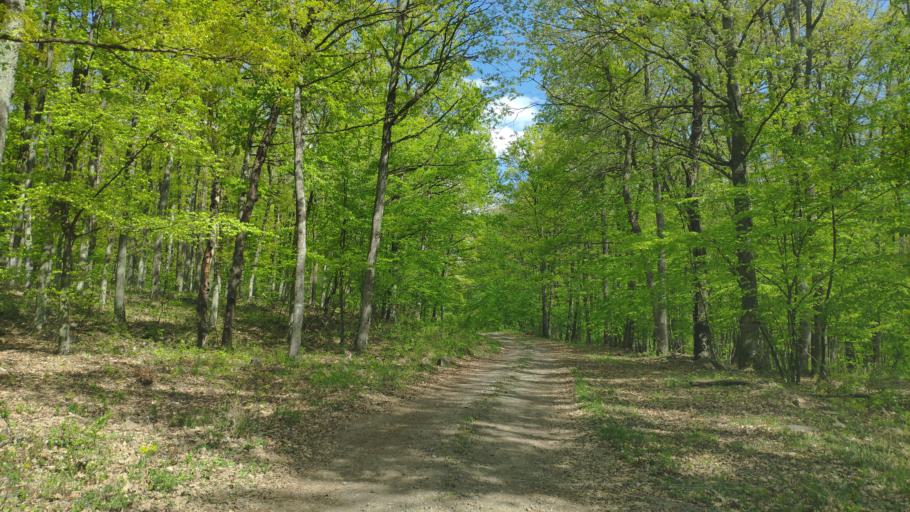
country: SK
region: Kosicky
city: Kosice
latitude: 48.6596
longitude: 21.4396
